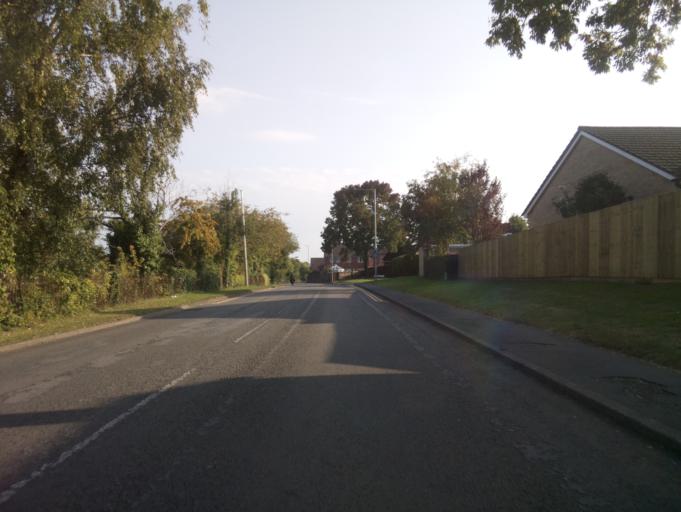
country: GB
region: Wales
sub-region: Torfaen County Borough
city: New Inn
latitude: 51.6833
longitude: -3.0218
